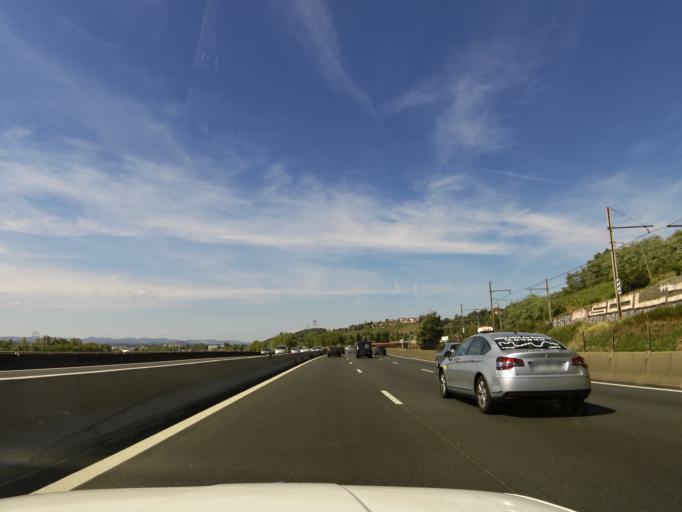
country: FR
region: Rhone-Alpes
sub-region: Departement du Rhone
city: Loire-sur-Rhone
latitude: 45.5649
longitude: 4.8180
